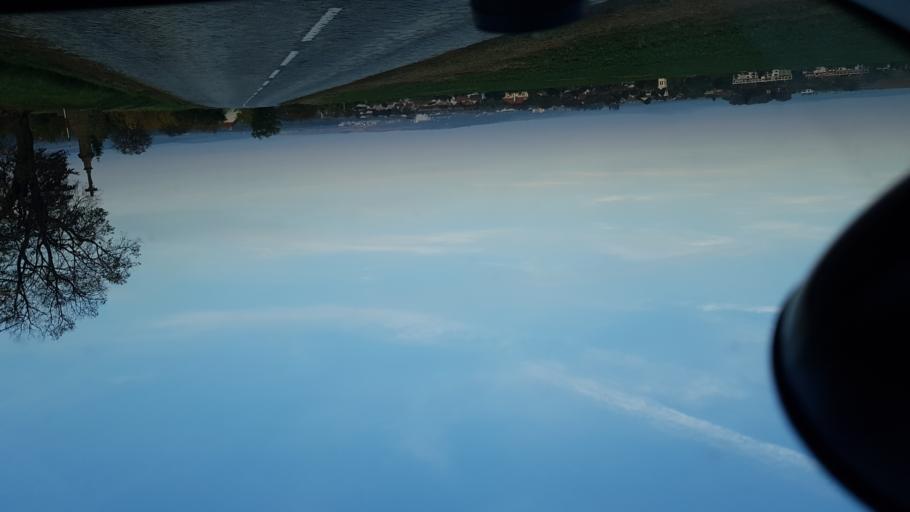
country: CZ
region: Zlin
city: Zlechov
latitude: 49.0713
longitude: 17.3723
